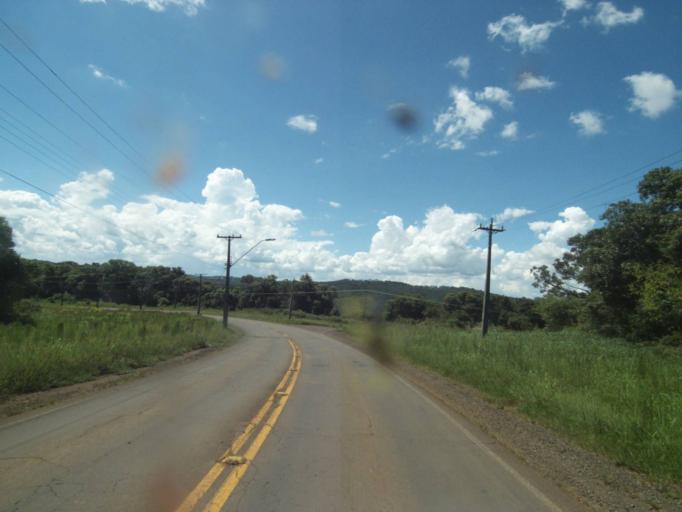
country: BR
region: Parana
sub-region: Chopinzinho
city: Chopinzinho
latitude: -25.7806
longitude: -52.1011
